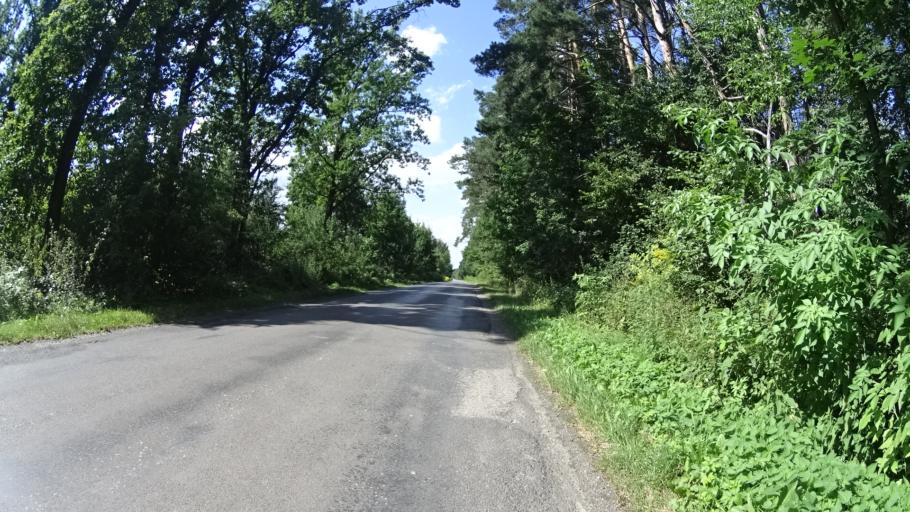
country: PL
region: Masovian Voivodeship
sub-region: Powiat grojecki
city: Mogielnica
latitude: 51.6929
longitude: 20.7359
